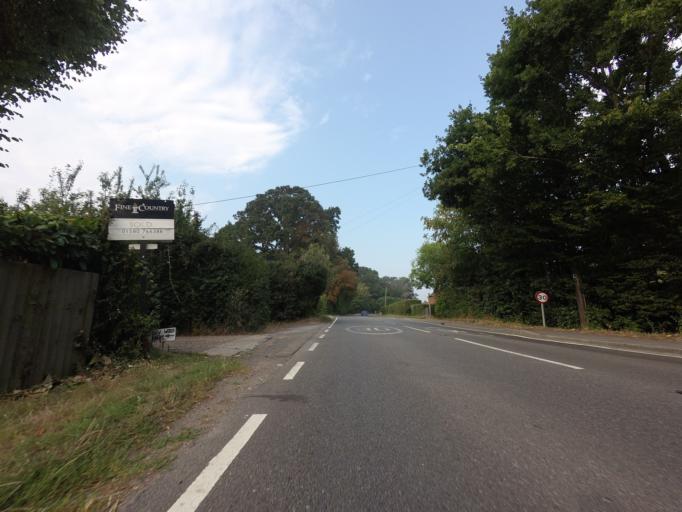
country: GB
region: England
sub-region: Kent
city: Tenterden
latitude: 51.1265
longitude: 0.7541
